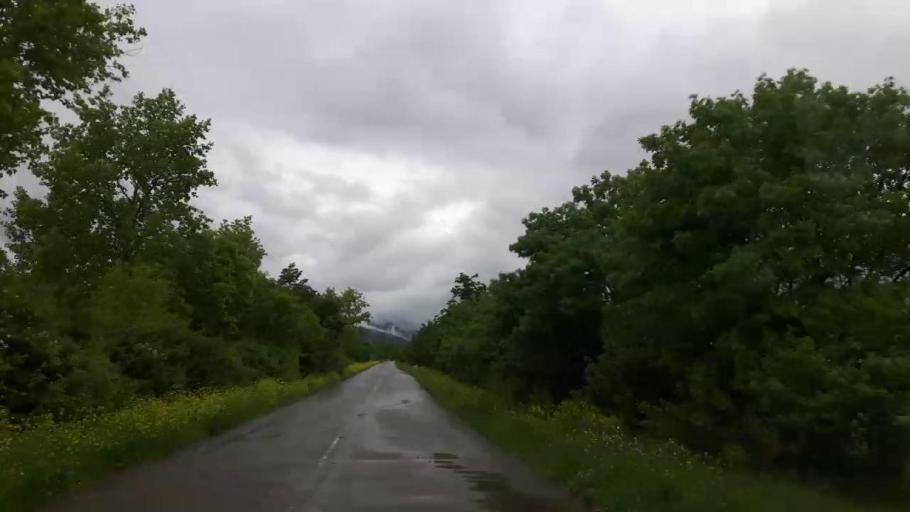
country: GE
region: Shida Kartli
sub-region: Khashuris Raioni
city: Khashuri
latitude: 41.9833
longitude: 43.6758
